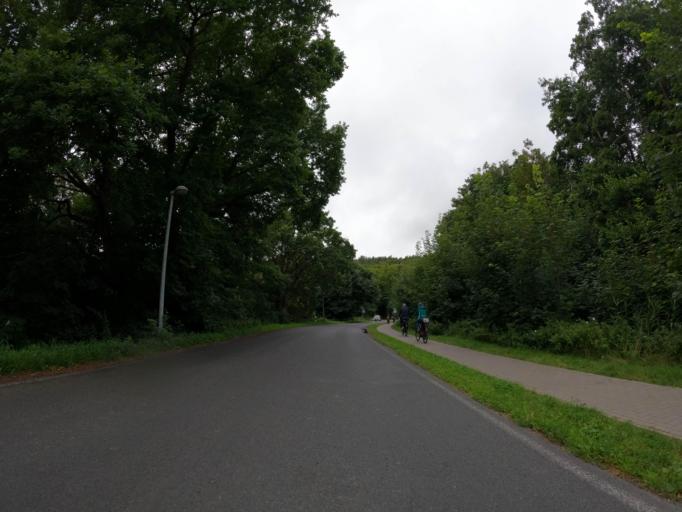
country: DE
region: Mecklenburg-Vorpommern
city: Ostseebad Gohren
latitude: 54.3027
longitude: 13.7038
